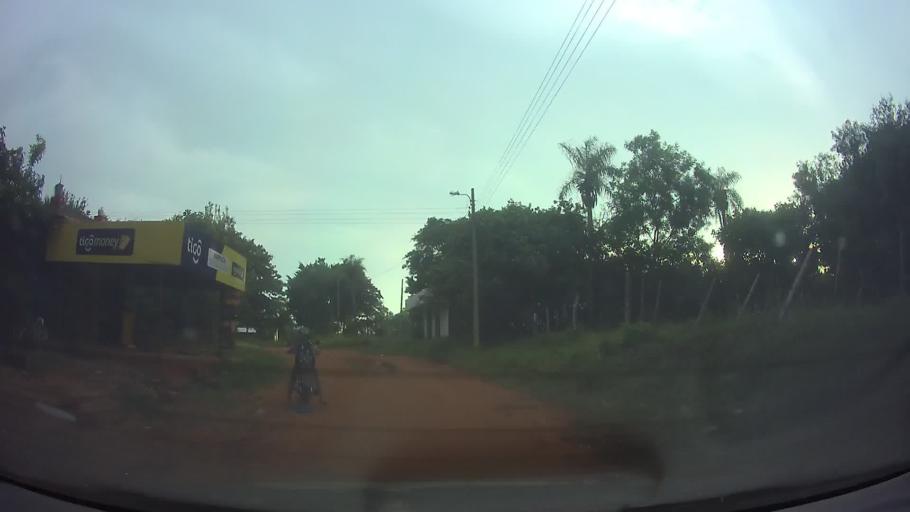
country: PY
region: Central
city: Limpio
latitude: -25.2435
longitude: -57.4492
